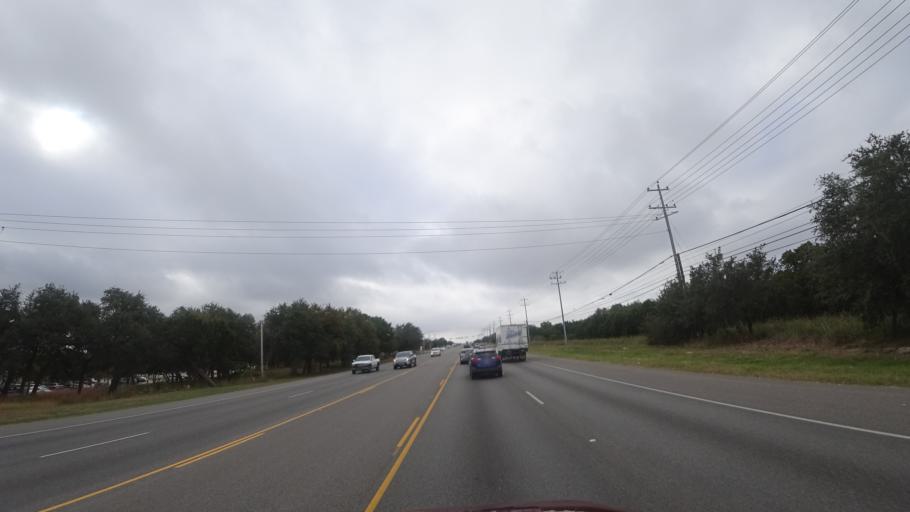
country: US
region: Texas
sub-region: Williamson County
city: Anderson Mill
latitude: 30.4305
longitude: -97.8421
